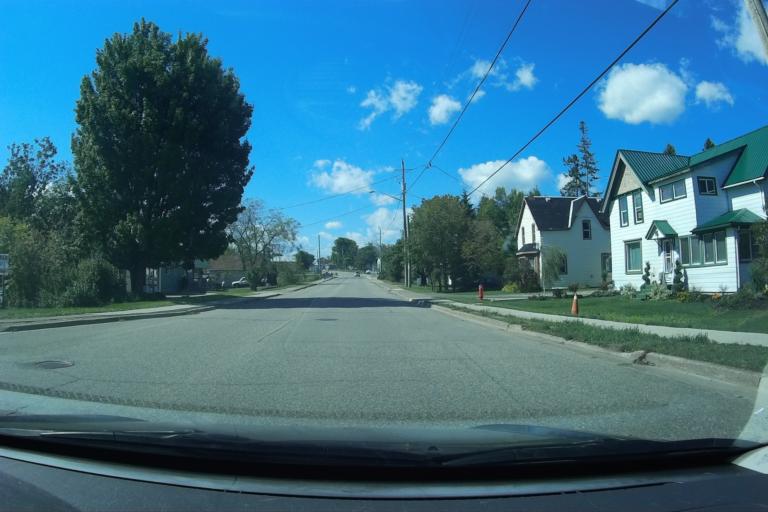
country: CA
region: Ontario
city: Thessalon
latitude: 46.2567
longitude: -83.5582
